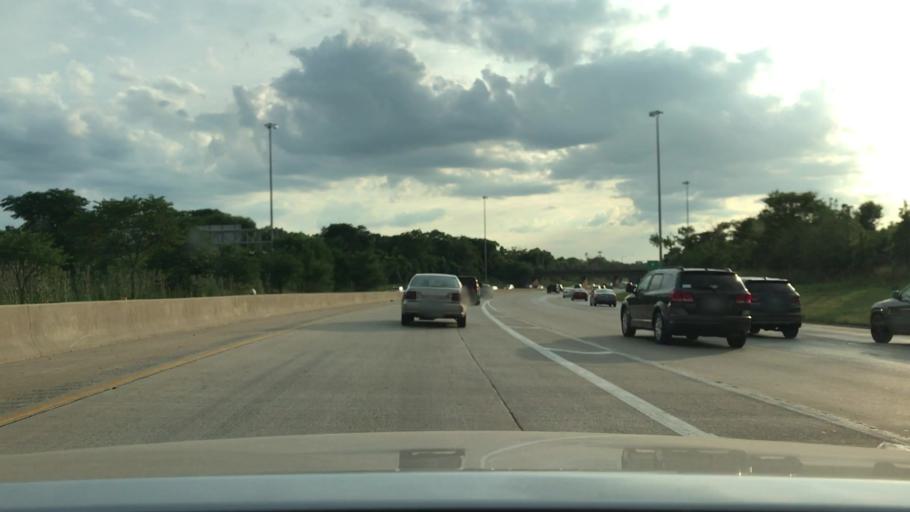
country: US
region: Illinois
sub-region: Cook County
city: Calumet Park
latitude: 41.7153
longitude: -87.6292
